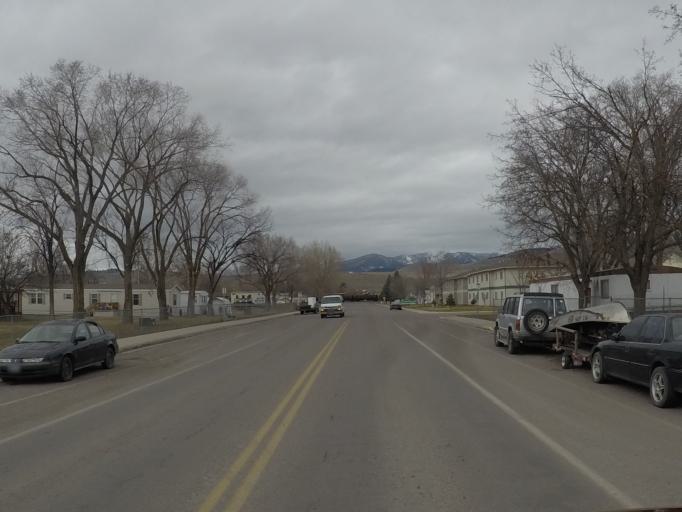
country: US
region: Montana
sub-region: Missoula County
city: Missoula
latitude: 46.8855
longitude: -114.0185
